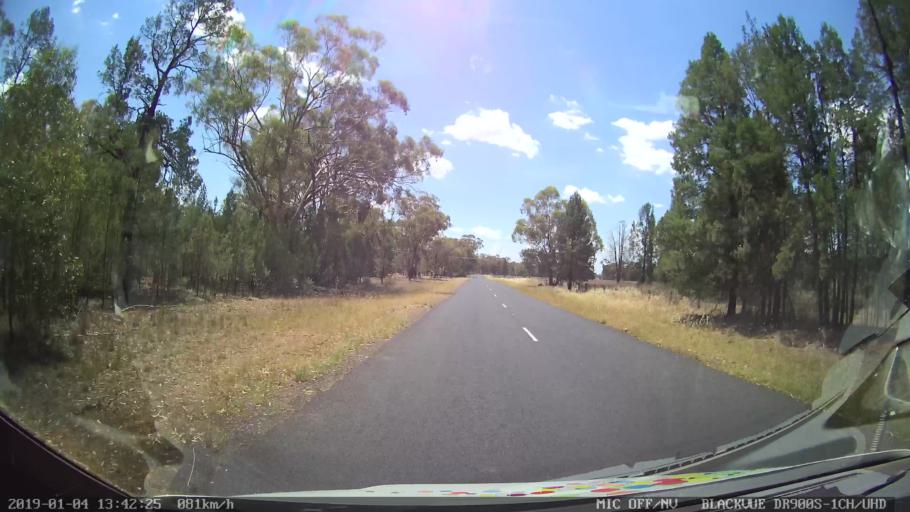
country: AU
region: New South Wales
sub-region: Dubbo Municipality
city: Dubbo
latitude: -32.4900
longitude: 148.5553
